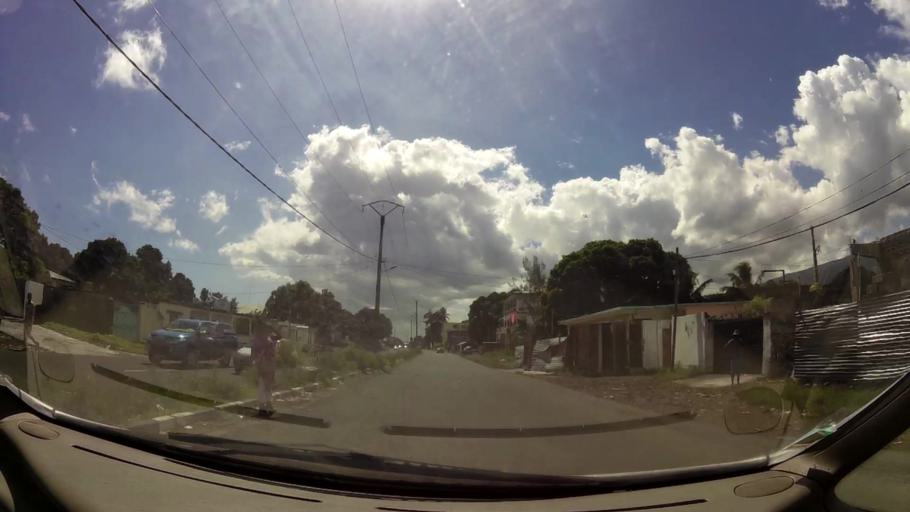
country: KM
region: Grande Comore
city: Mavingouni
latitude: -11.7143
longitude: 43.2461
